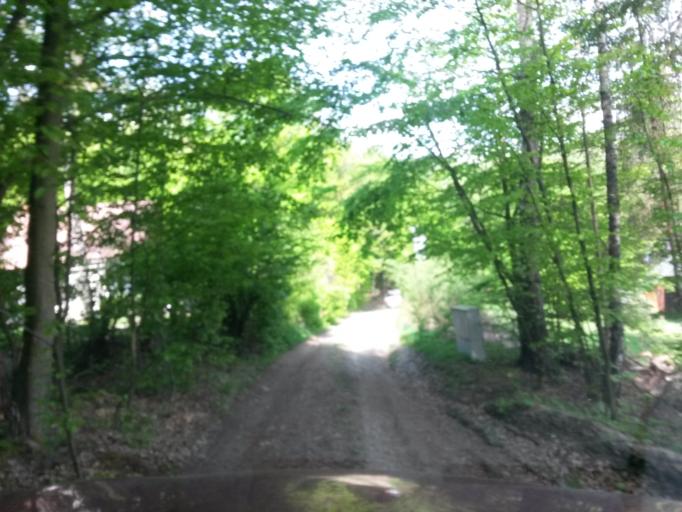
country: SK
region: Kosicky
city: Gelnica
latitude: 48.8322
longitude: 21.0662
